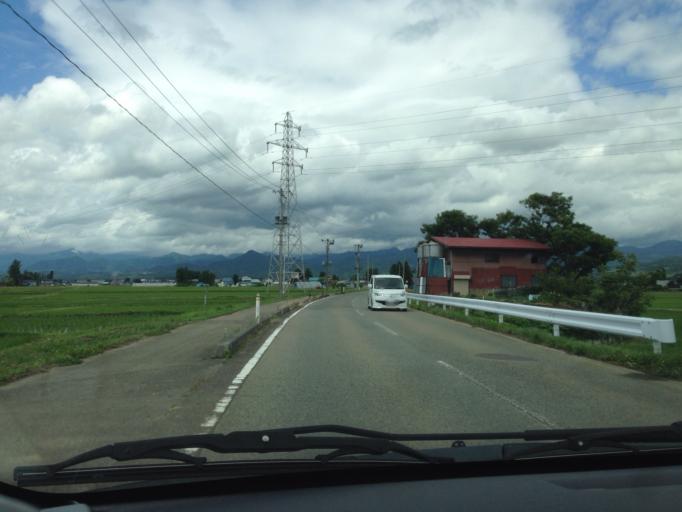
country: JP
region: Fukushima
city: Kitakata
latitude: 37.6187
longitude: 139.9001
